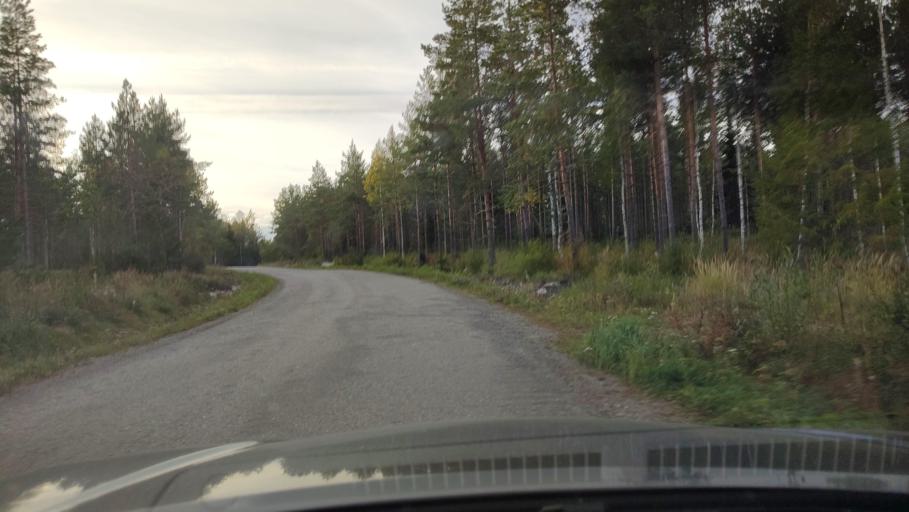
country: FI
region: Ostrobothnia
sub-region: Sydosterbotten
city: Kristinestad
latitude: 62.1502
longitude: 21.5494
